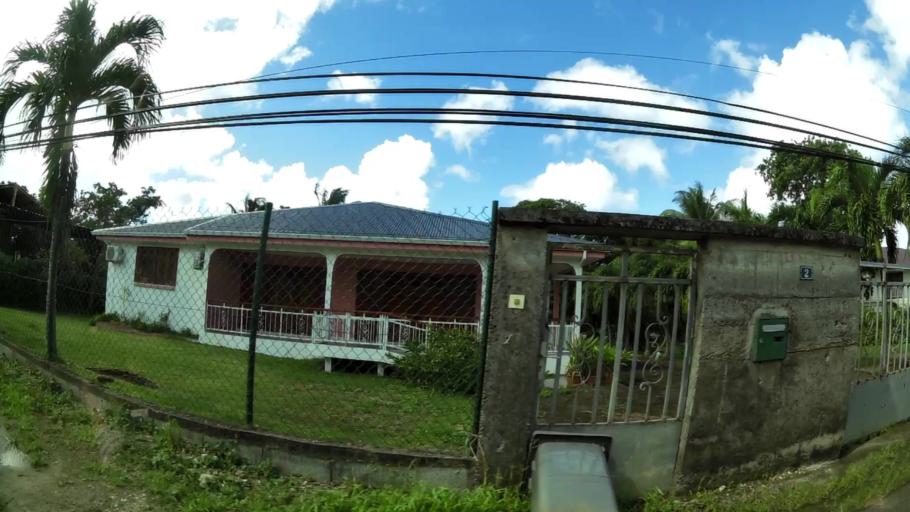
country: GP
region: Guadeloupe
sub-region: Guadeloupe
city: Anse-Bertrand
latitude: 16.4670
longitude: -61.5049
